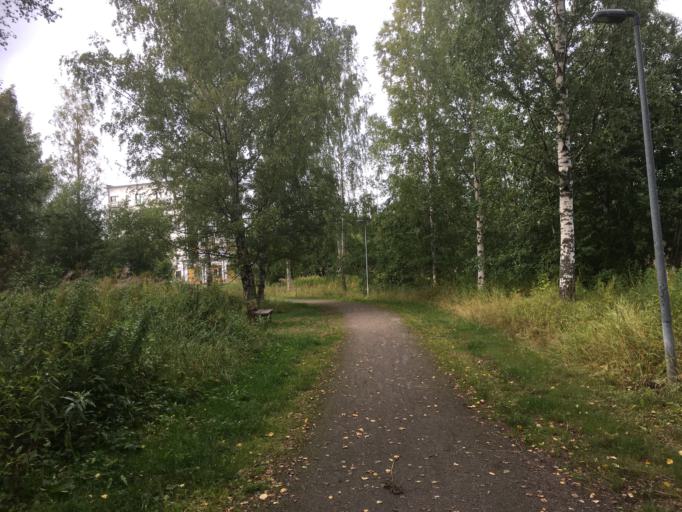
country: FI
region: Central Finland
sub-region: Jyvaeskylae
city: Jyvaeskylae
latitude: 62.2252
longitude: 25.7925
